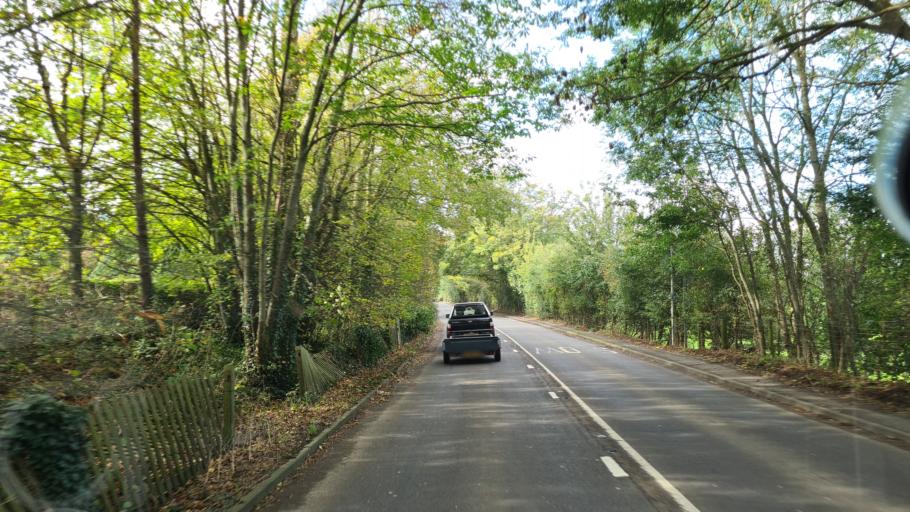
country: GB
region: England
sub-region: East Sussex
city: Bodle Street
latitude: 50.8832
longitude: 0.3516
